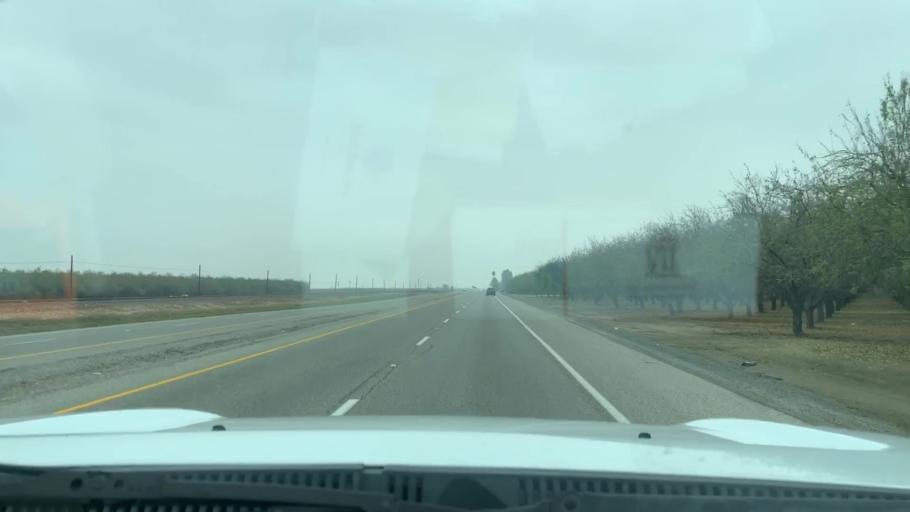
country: US
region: California
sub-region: Kern County
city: Shafter
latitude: 35.5329
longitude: -119.3109
